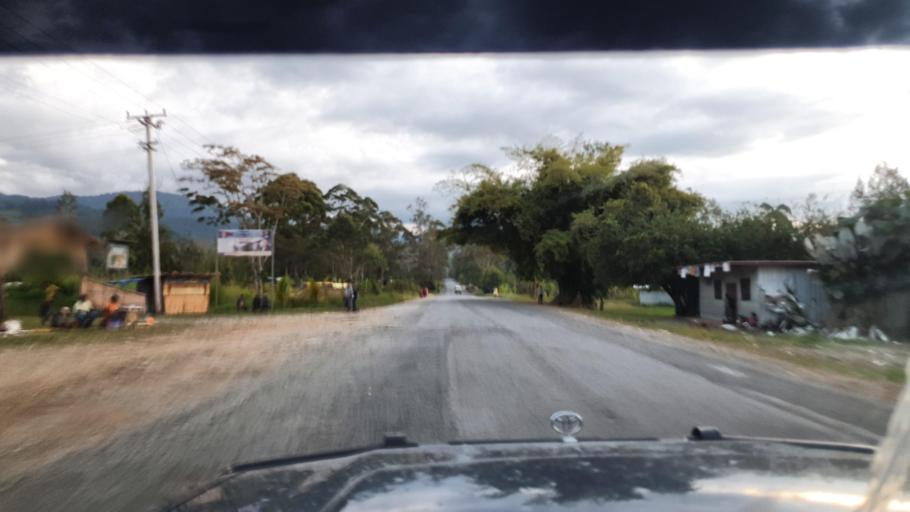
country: PG
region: Jiwaka
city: Minj
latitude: -5.8364
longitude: 144.5426
